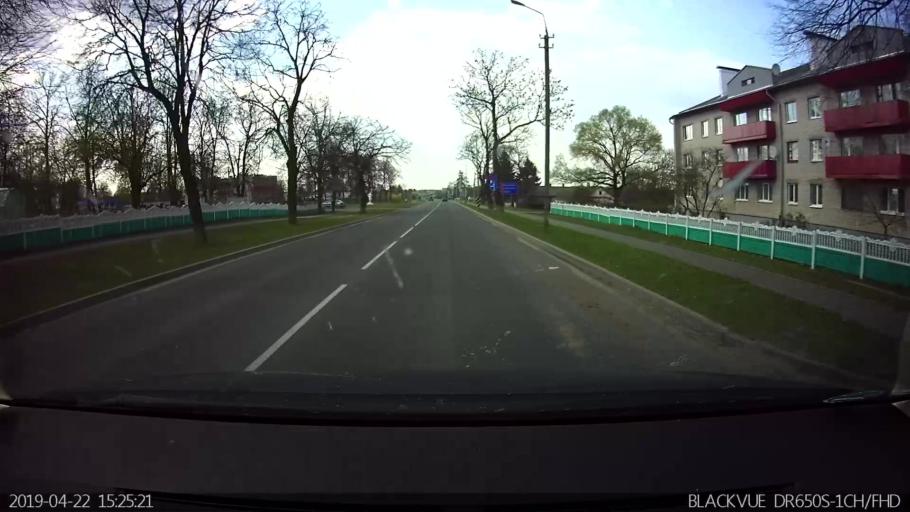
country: BY
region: Brest
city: Vysokaye
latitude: 52.3642
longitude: 23.3966
